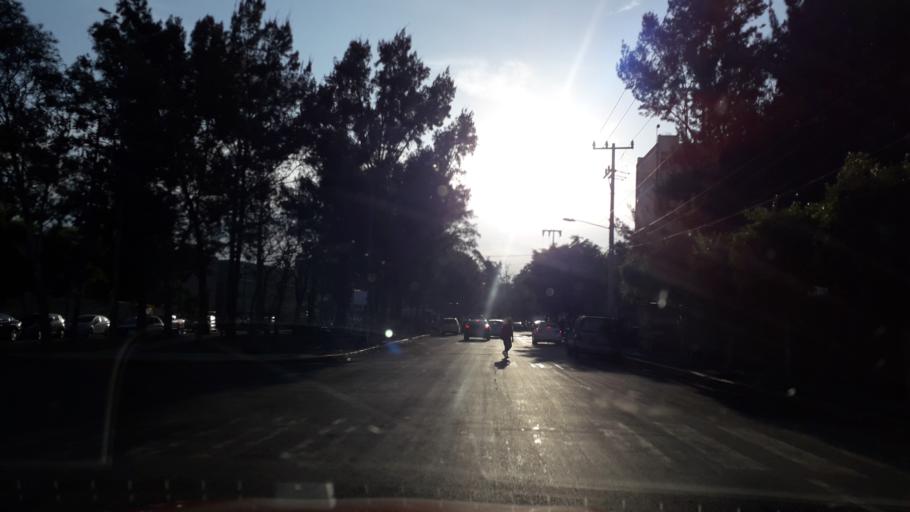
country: MX
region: Mexico City
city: Iztapalapa
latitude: 19.3585
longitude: -99.0528
